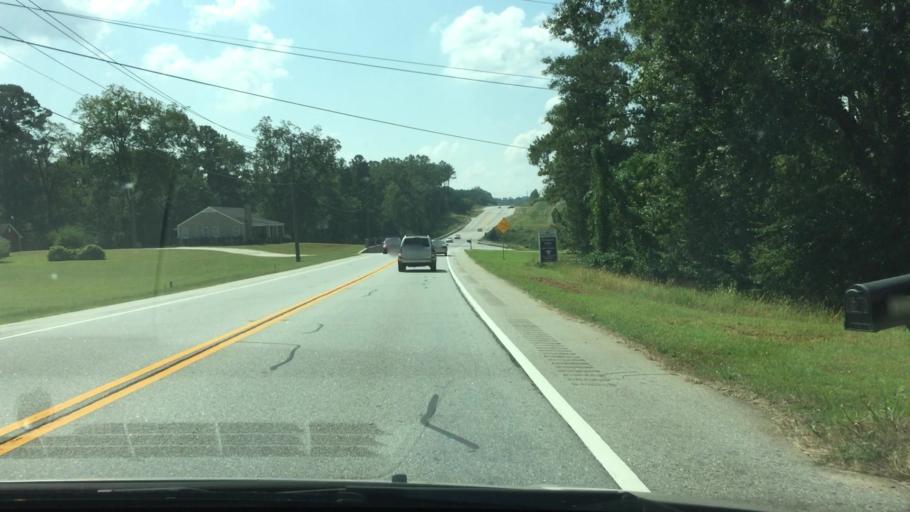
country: US
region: Georgia
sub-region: Henry County
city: McDonough
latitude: 33.5362
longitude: -84.1388
